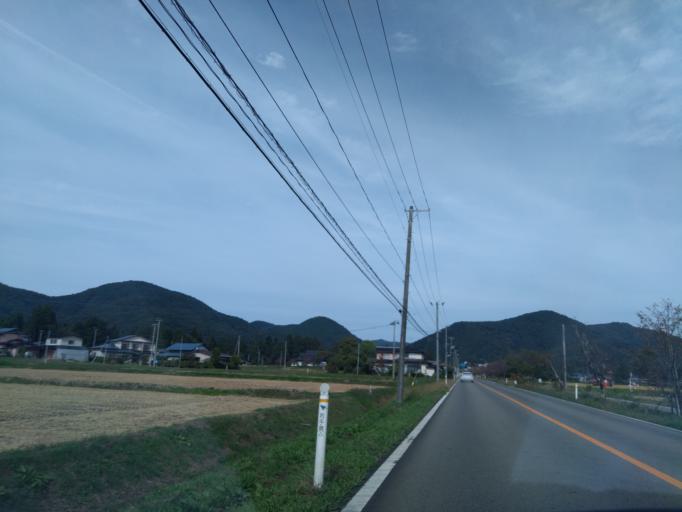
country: JP
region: Iwate
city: Hanamaki
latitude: 39.4407
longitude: 141.0776
